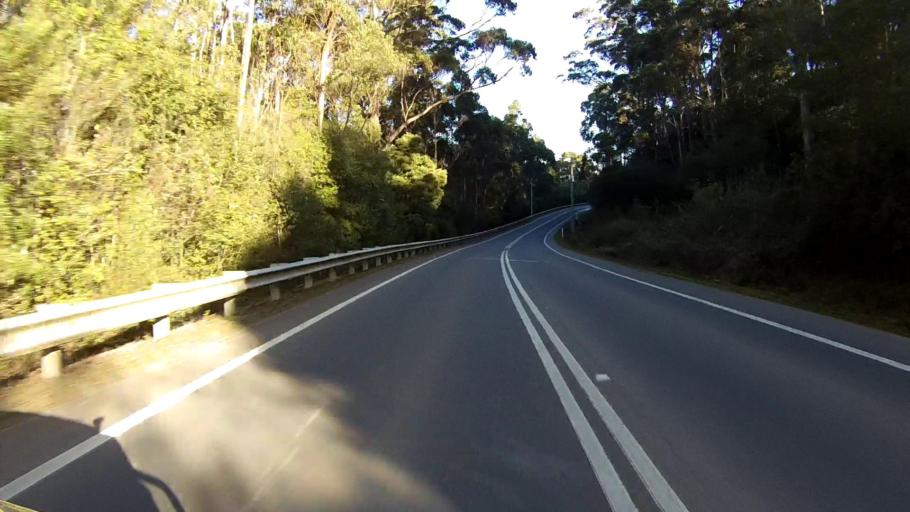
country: AU
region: Tasmania
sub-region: Clarence
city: Sandford
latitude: -43.1147
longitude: 147.8555
